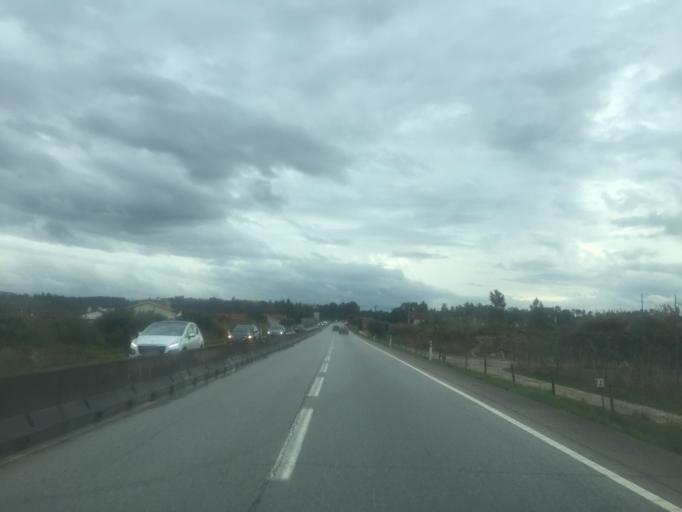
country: PT
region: Aveiro
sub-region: Mealhada
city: Pampilhosa do Botao
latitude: 40.2930
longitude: -8.4302
